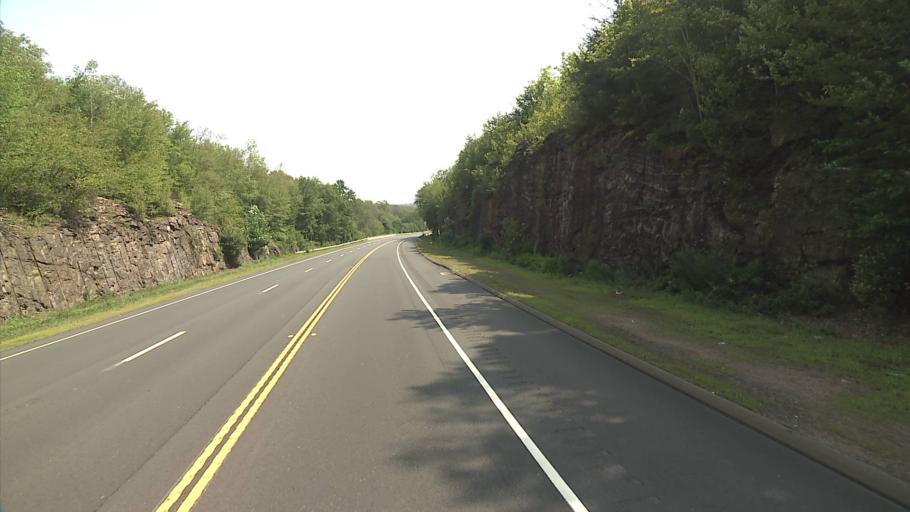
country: US
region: Connecticut
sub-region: Middlesex County
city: East Haddam
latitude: 41.4398
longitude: -72.4829
